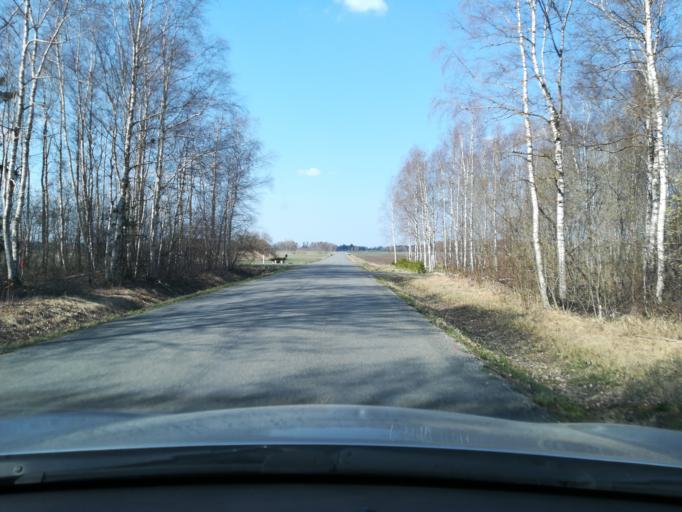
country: EE
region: Harju
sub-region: Saue linn
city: Saue
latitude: 59.3296
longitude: 24.5304
